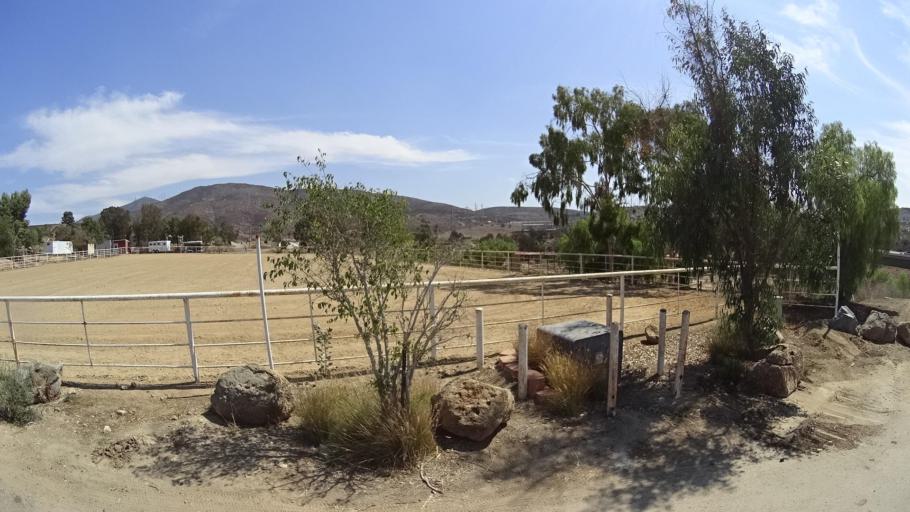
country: US
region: California
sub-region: San Diego County
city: La Presa
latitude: 32.6826
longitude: -116.9887
